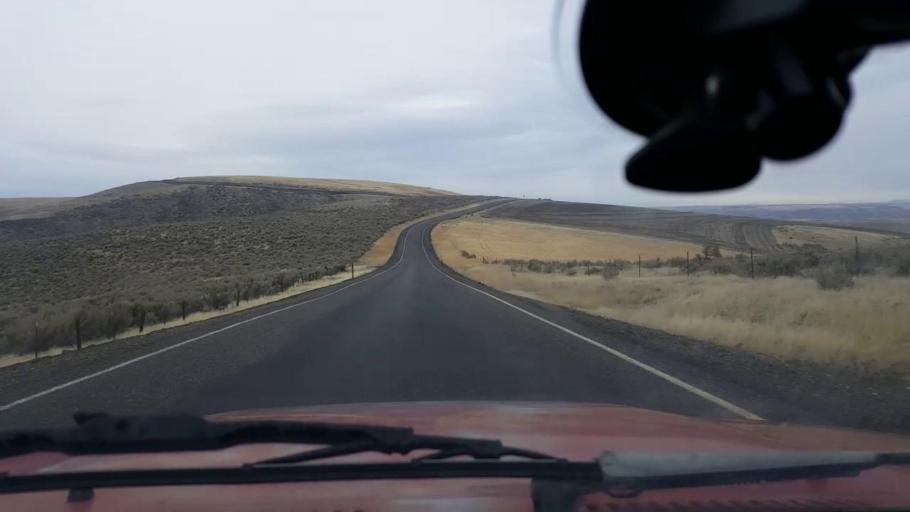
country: US
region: Washington
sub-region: Asotin County
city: Clarkston Heights-Vineland
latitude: 46.3135
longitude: -117.3424
